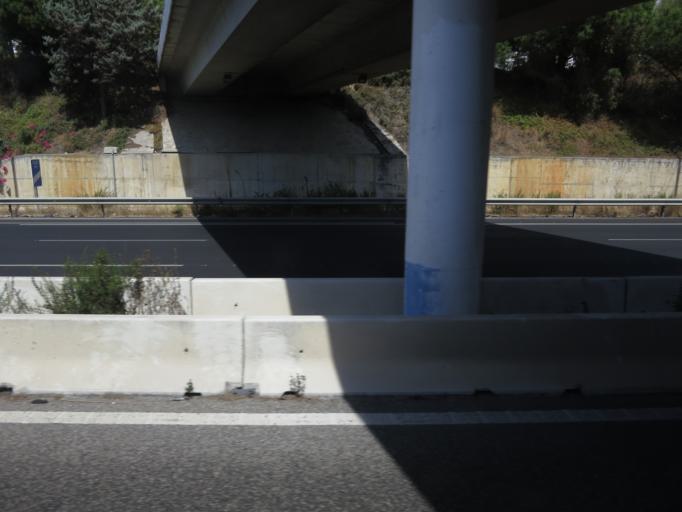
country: ES
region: Andalusia
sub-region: Provincia de Malaga
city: Marbella
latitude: 36.5134
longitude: -4.9208
